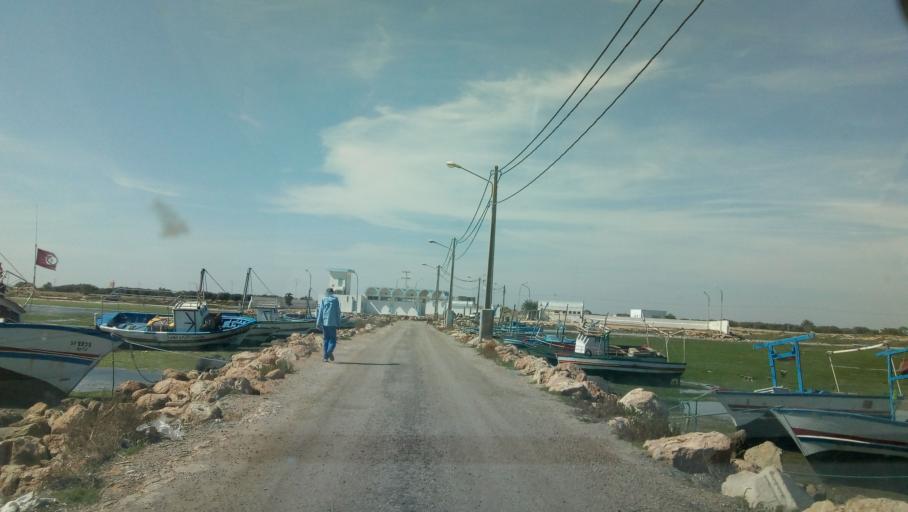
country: TN
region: Safaqis
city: Jabinyanah
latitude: 34.8701
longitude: 10.9107
